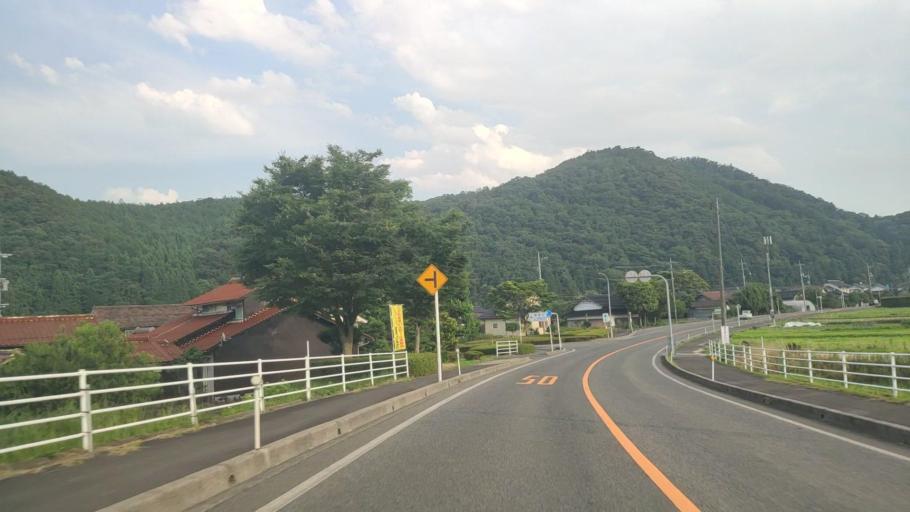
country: JP
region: Tottori
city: Kurayoshi
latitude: 35.3882
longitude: 133.7807
